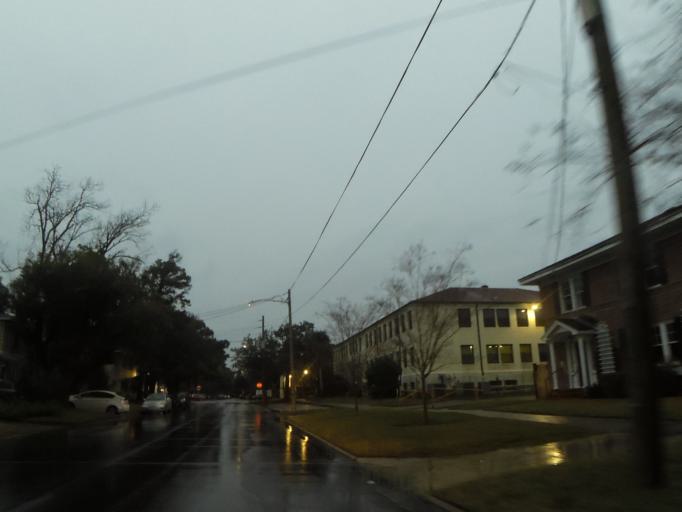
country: US
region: Florida
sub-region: Duval County
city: Jacksonville
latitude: 30.3104
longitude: -81.6922
